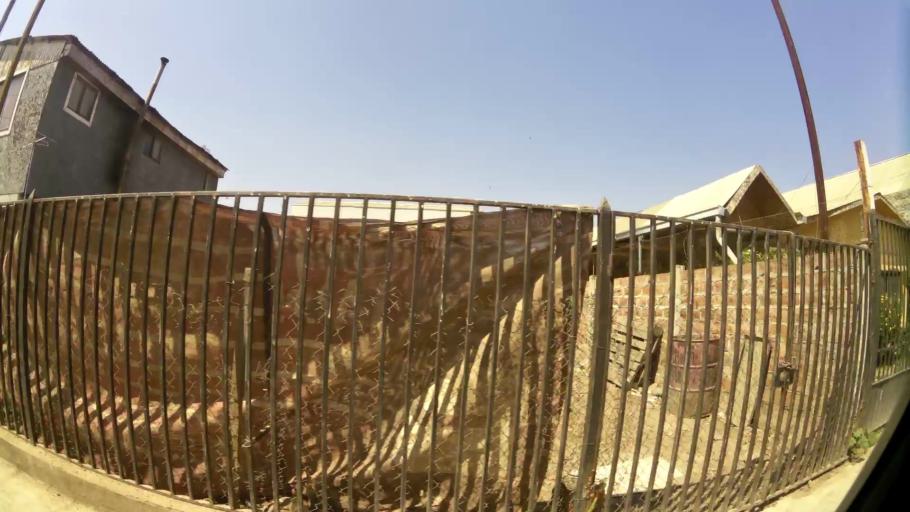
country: CL
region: Santiago Metropolitan
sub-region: Provincia de Talagante
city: Penaflor
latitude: -33.5847
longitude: -70.8131
